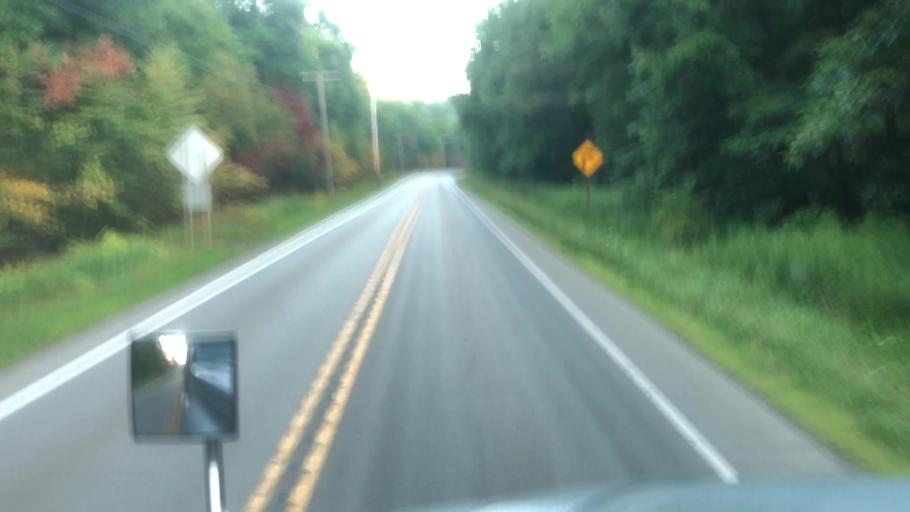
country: US
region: Pennsylvania
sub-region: Venango County
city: Hasson Heights
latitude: 41.4807
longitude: -79.6615
